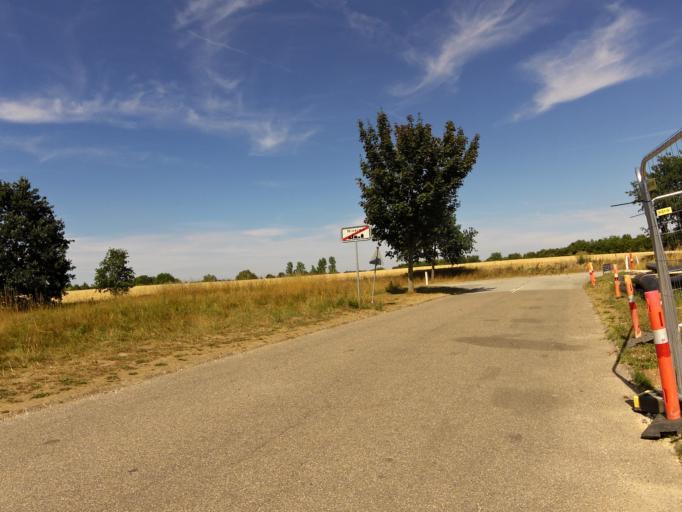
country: DK
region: Capital Region
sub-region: Fredensborg Kommune
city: Niva
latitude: 55.9462
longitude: 12.4983
